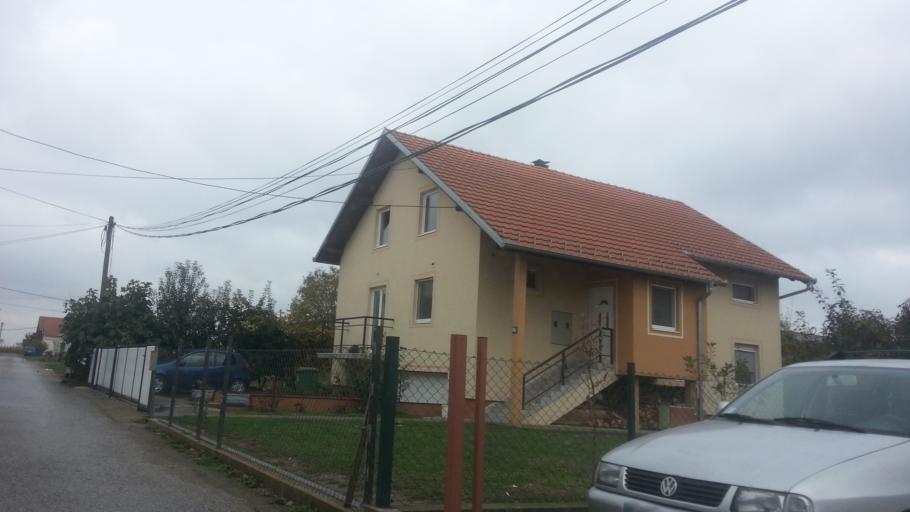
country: RS
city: Novi Banovci
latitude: 44.9134
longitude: 20.2883
